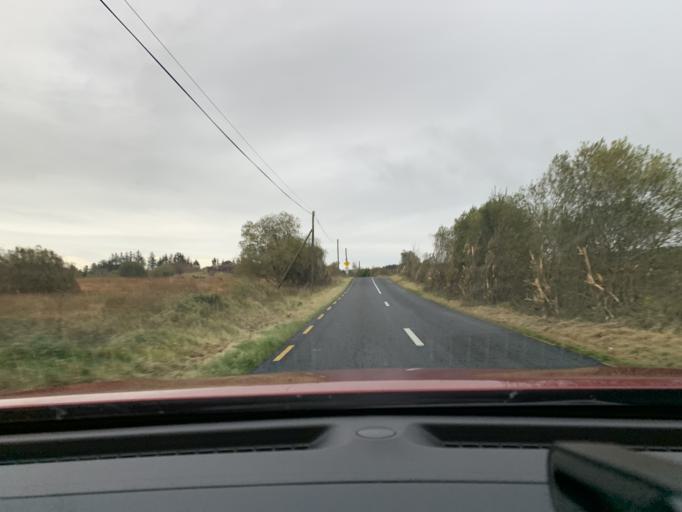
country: IE
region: Connaught
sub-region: Roscommon
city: Ballaghaderreen
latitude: 53.9462
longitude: -8.5457
